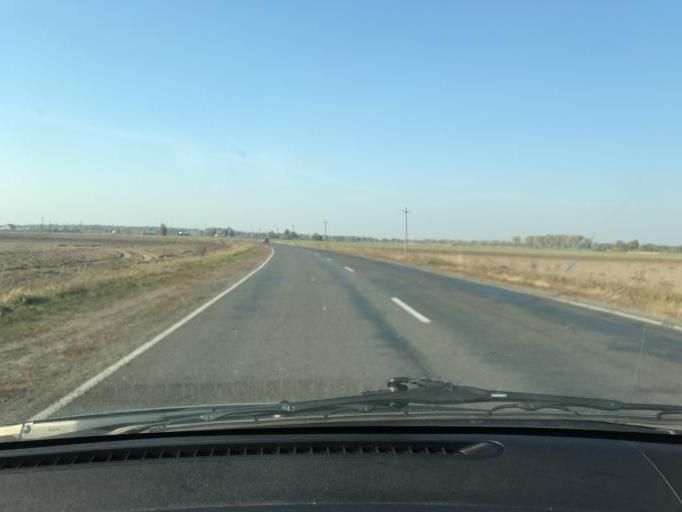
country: BY
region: Brest
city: Davyd-Haradok
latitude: 52.0673
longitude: 27.2513
